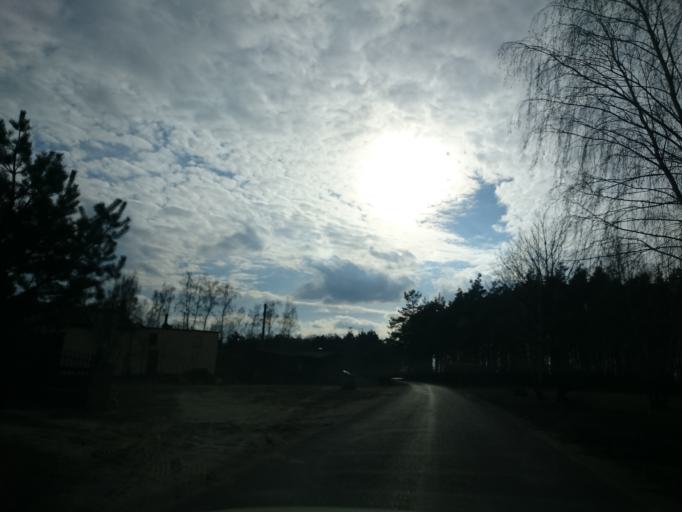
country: PL
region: Kujawsko-Pomorskie
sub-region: Powiat torunski
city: Lubicz Gorny
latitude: 53.0503
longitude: 18.8370
